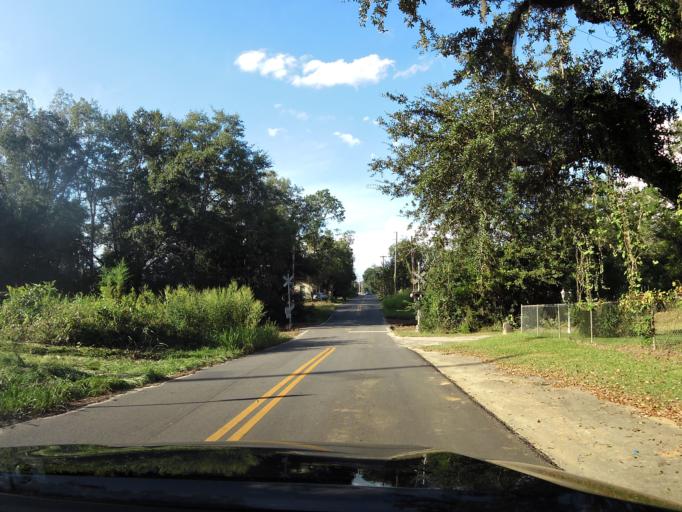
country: US
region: Georgia
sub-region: Brooks County
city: Quitman
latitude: 30.7811
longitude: -83.5529
